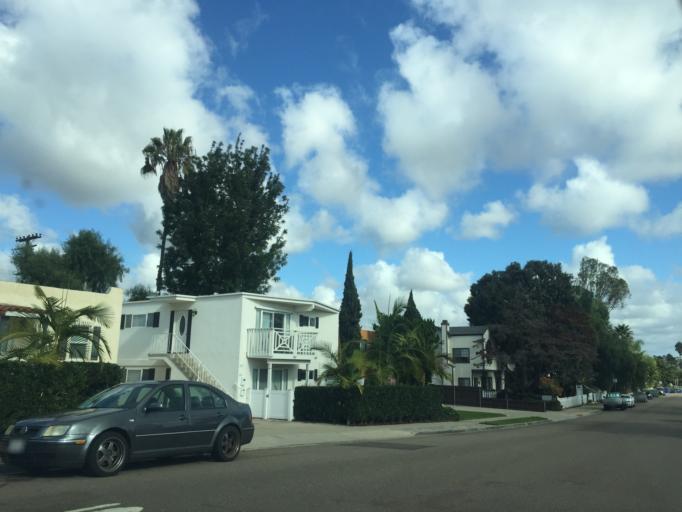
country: US
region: California
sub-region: San Diego County
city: La Jolla
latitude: 32.7981
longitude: -117.2344
